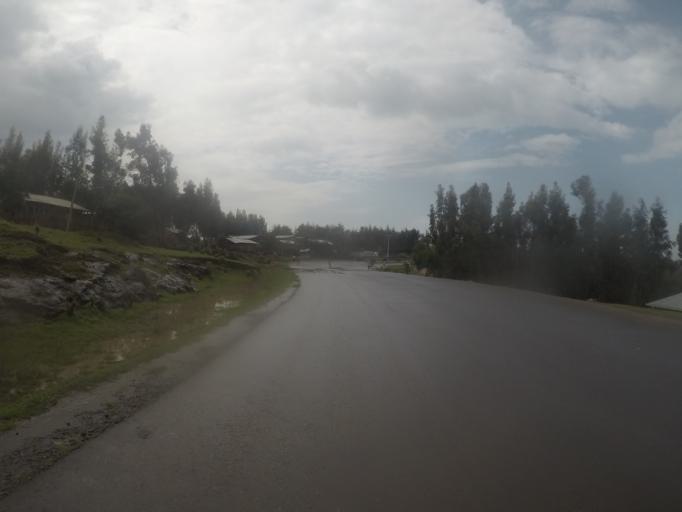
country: ET
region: Amhara
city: Debark'
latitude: 13.1400
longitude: 37.8940
